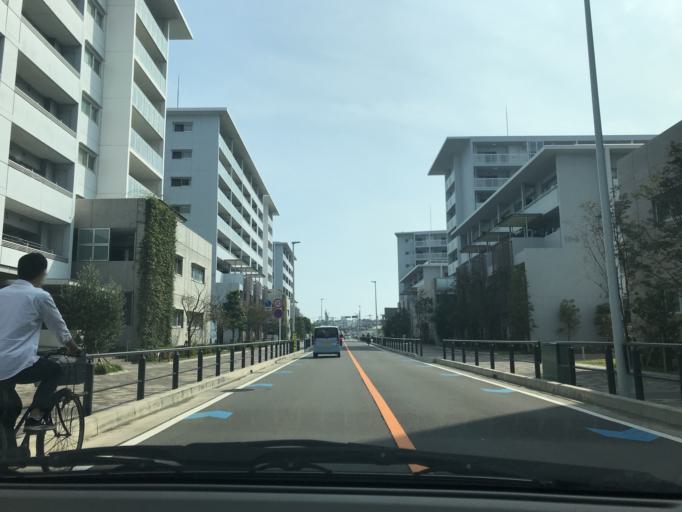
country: JP
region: Kanagawa
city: Chigasaki
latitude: 35.3254
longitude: 139.3885
